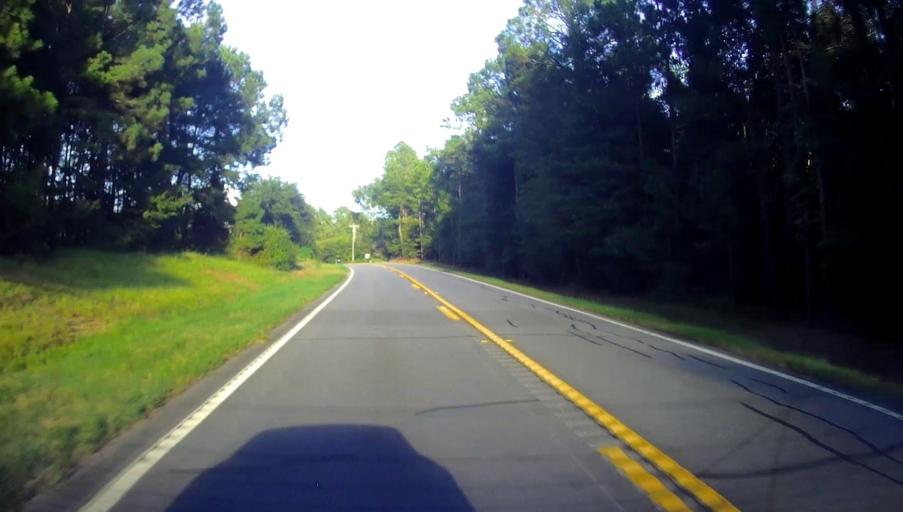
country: US
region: Georgia
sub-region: Pulaski County
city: Hawkinsville
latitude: 32.2650
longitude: -83.5227
